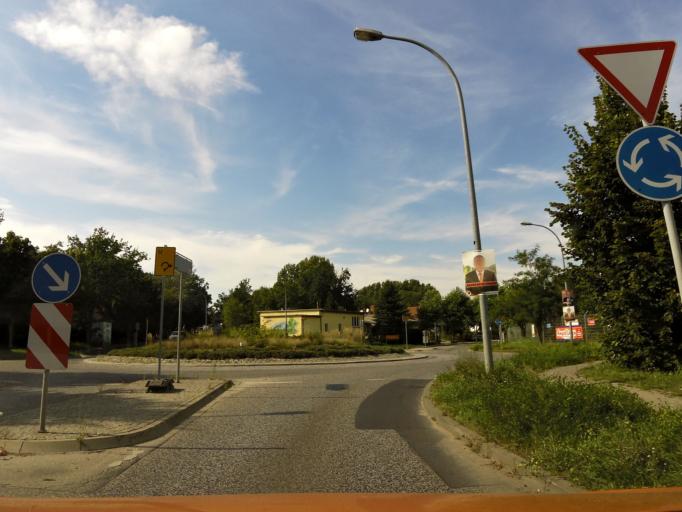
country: DE
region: Brandenburg
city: Teltow
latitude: 52.3813
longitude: 13.2483
